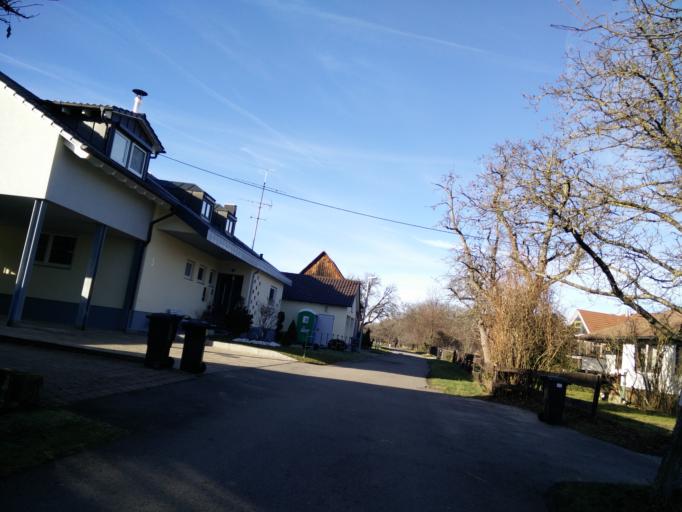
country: DE
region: Baden-Wuerttemberg
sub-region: Tuebingen Region
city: Gomaringen
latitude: 48.4737
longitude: 9.0822
